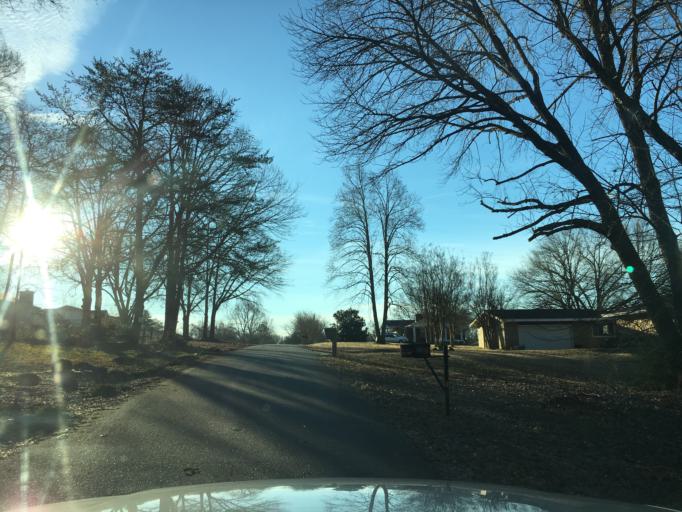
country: US
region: South Carolina
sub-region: Spartanburg County
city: Lyman
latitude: 34.9248
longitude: -82.1256
